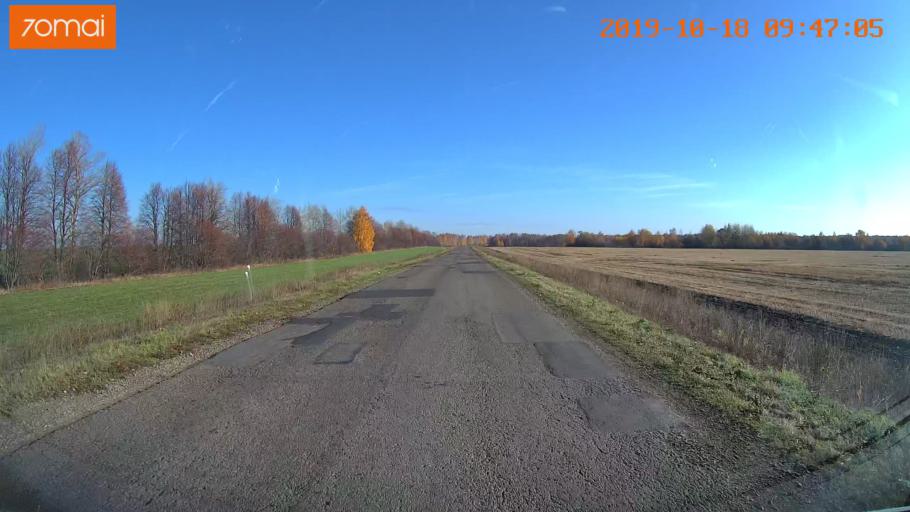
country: RU
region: Tula
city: Kazachka
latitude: 53.3153
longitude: 38.2251
